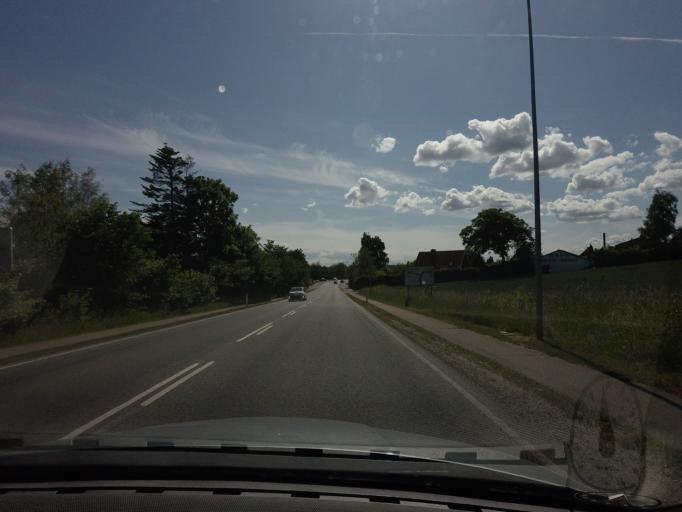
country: DK
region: Central Jutland
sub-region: Syddjurs Kommune
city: Ebeltoft
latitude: 56.3030
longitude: 10.6897
